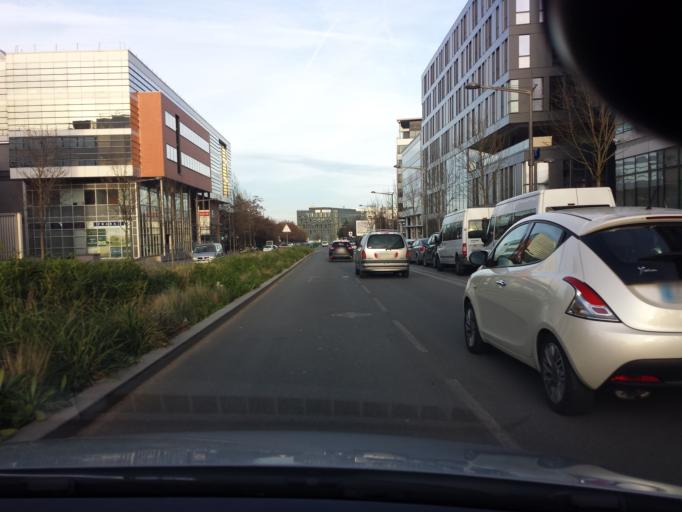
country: FR
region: Ile-de-France
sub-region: Departement de l'Essonne
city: Palaiseau
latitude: 48.7263
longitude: 2.2628
